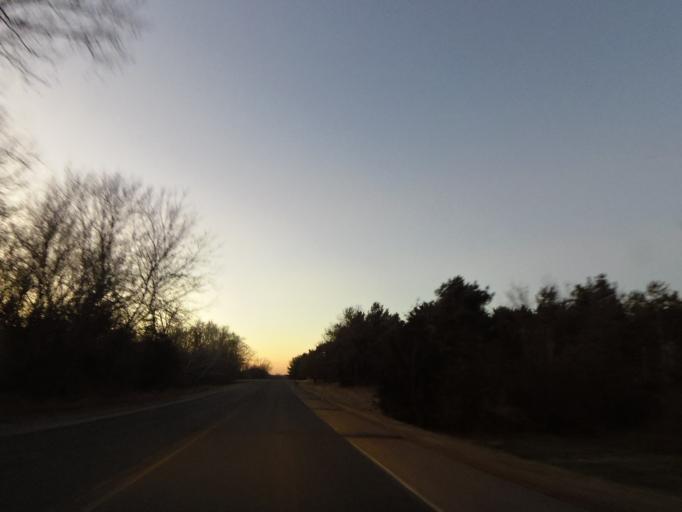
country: US
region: Minnesota
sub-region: Washington County
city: Lakeland
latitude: 44.9390
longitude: -92.7246
